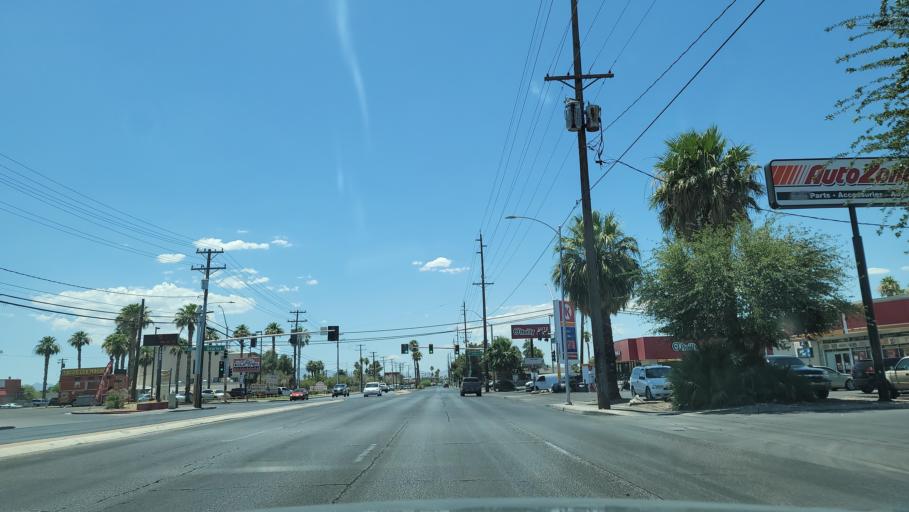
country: US
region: Nevada
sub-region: Clark County
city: North Las Vegas
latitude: 36.1856
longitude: -115.1162
